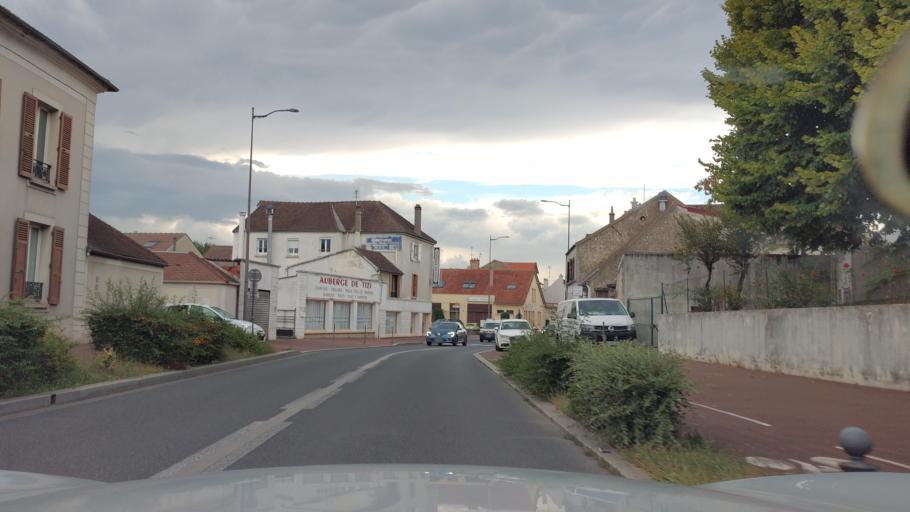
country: FR
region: Ile-de-France
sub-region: Departement de Seine-et-Marne
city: Brie-Comte-Robert
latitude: 48.6904
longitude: 2.6144
